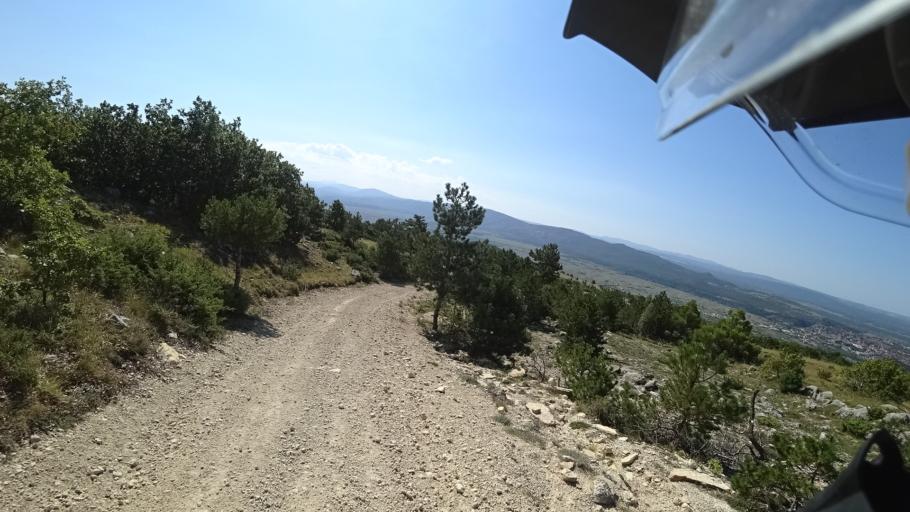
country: HR
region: Sibensko-Kniniska
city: Drnis
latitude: 43.8855
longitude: 16.1798
